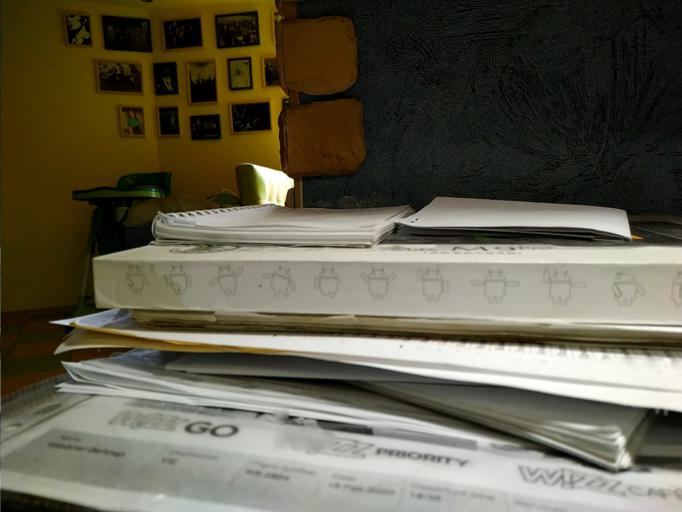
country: RU
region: Pskov
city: Plyussa
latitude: 58.6005
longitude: 29.4141
